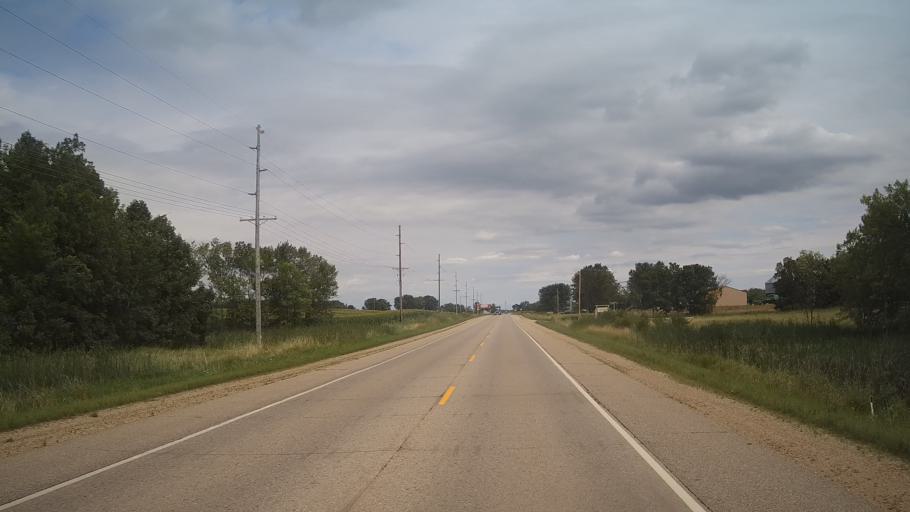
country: US
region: Wisconsin
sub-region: Green Lake County
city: Berlin
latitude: 44.0410
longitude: -88.9967
